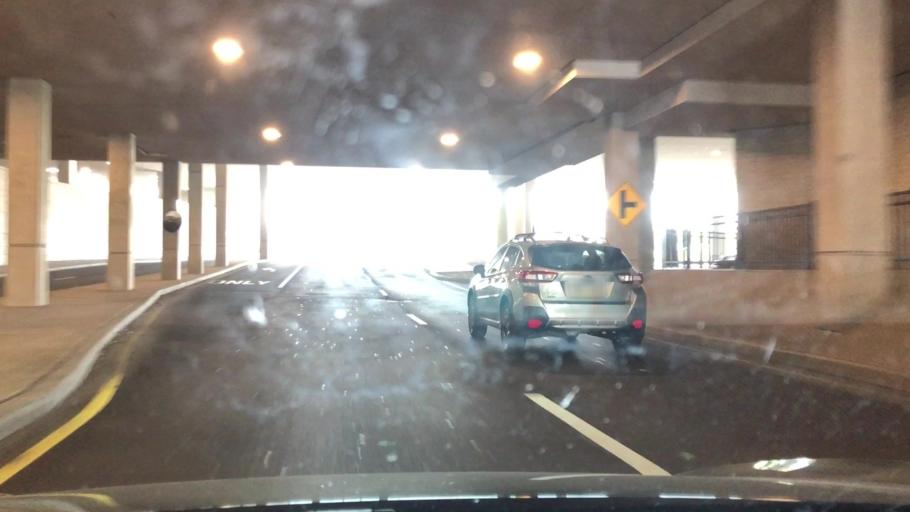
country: US
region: Pennsylvania
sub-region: Montgomery County
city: King of Prussia
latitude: 40.0884
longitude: -75.3883
